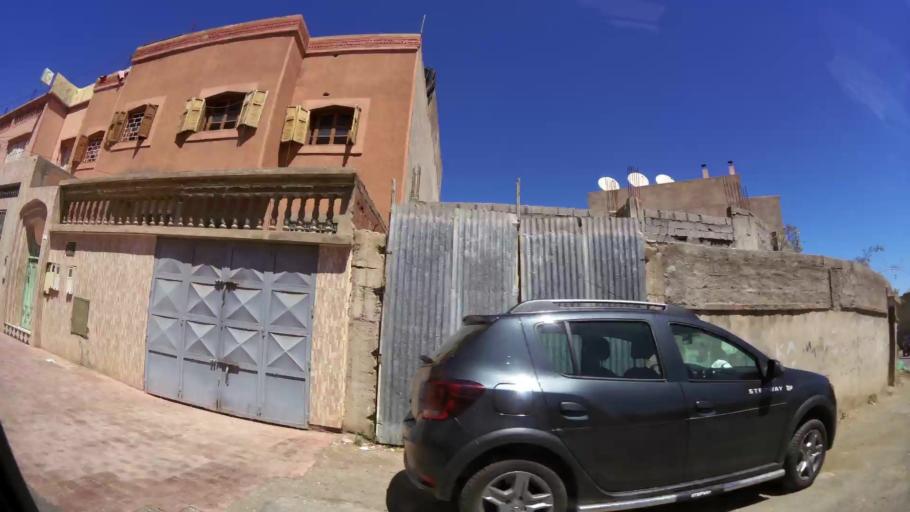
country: MA
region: Marrakech-Tensift-Al Haouz
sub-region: Marrakech
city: Marrakesh
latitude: 31.6541
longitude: -7.9885
